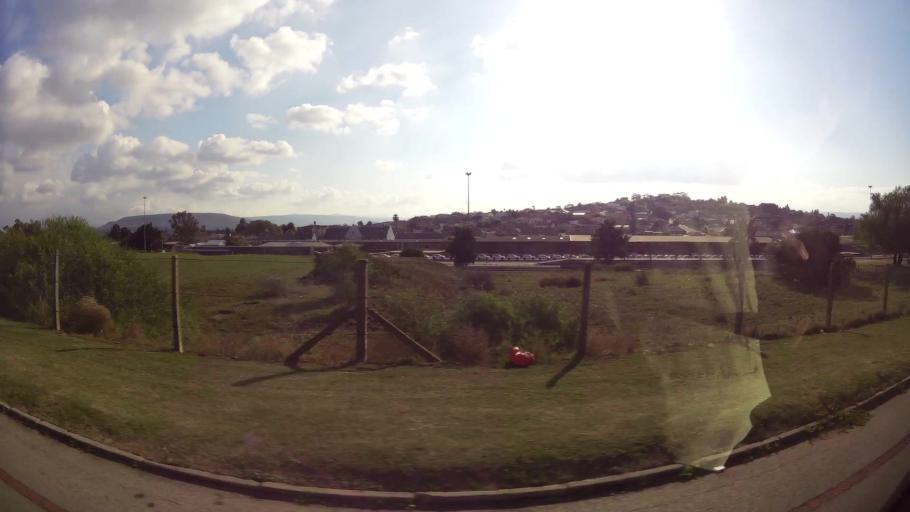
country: ZA
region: Eastern Cape
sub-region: Nelson Mandela Bay Metropolitan Municipality
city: Uitenhage
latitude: -33.7722
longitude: 25.4111
